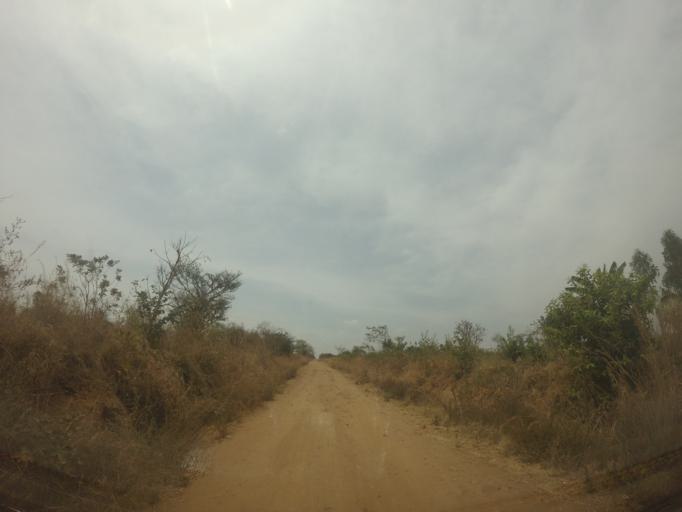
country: UG
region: Northern Region
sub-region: Nebbi District
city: Nebbi
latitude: 2.6327
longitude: 31.0339
